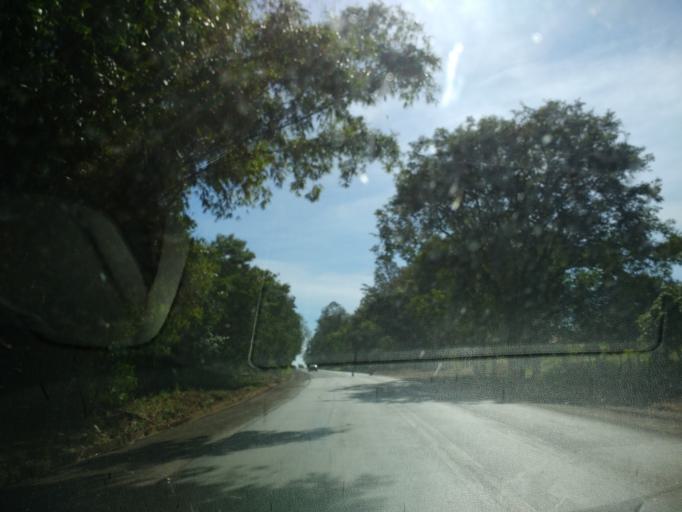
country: BR
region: Parana
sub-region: Umuarama
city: Umuarama
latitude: -23.8780
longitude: -53.3953
